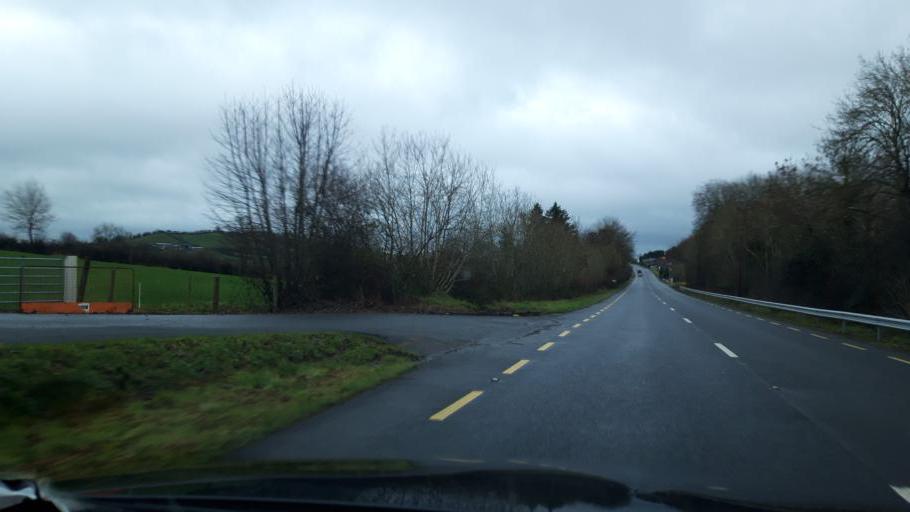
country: IE
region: Ulster
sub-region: County Monaghan
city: Castleblayney
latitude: 54.0901
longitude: -6.6955
